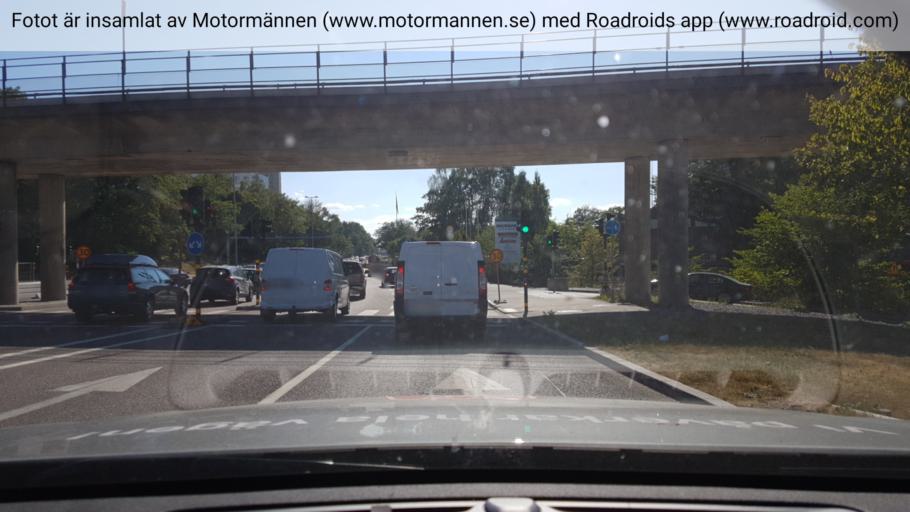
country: SE
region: Stockholm
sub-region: Stockholms Kommun
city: OEstermalm
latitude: 59.3504
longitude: 18.0984
